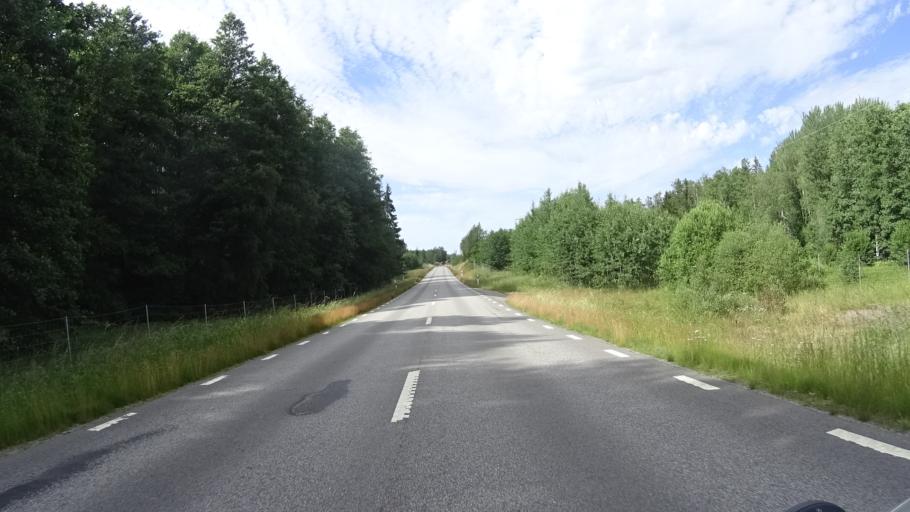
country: SE
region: OEstergoetland
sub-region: Atvidabergs Kommun
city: Atvidaberg
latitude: 58.1581
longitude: 16.0671
